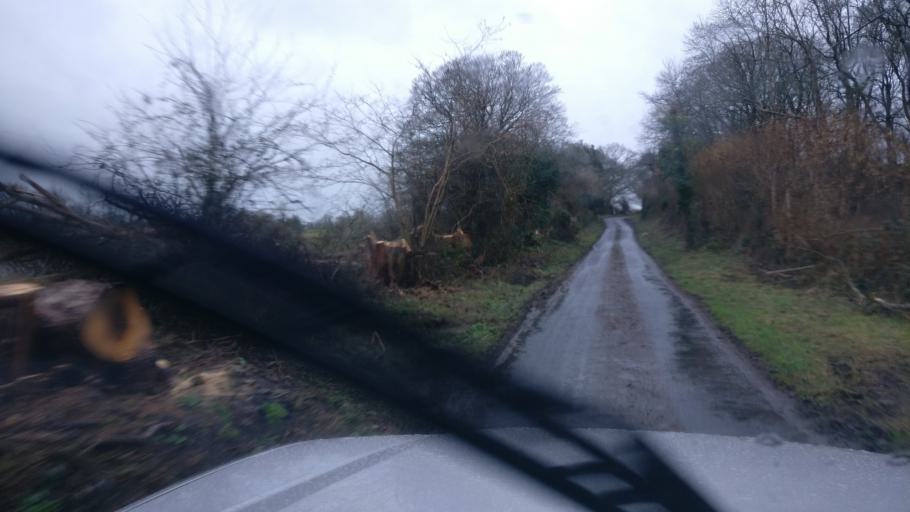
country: IE
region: Connaught
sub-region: County Galway
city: Ballinasloe
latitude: 53.2897
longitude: -8.2788
